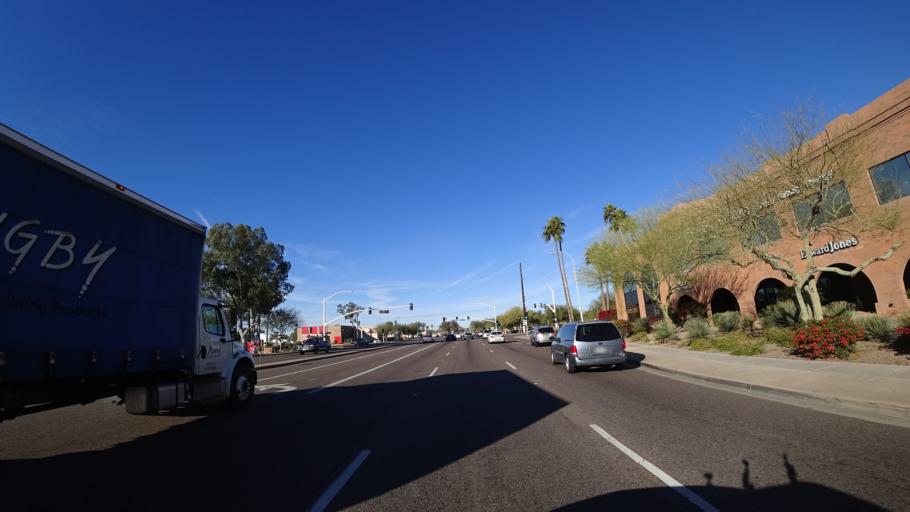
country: US
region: Arizona
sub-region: Maricopa County
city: Scottsdale
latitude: 33.4659
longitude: -111.9077
